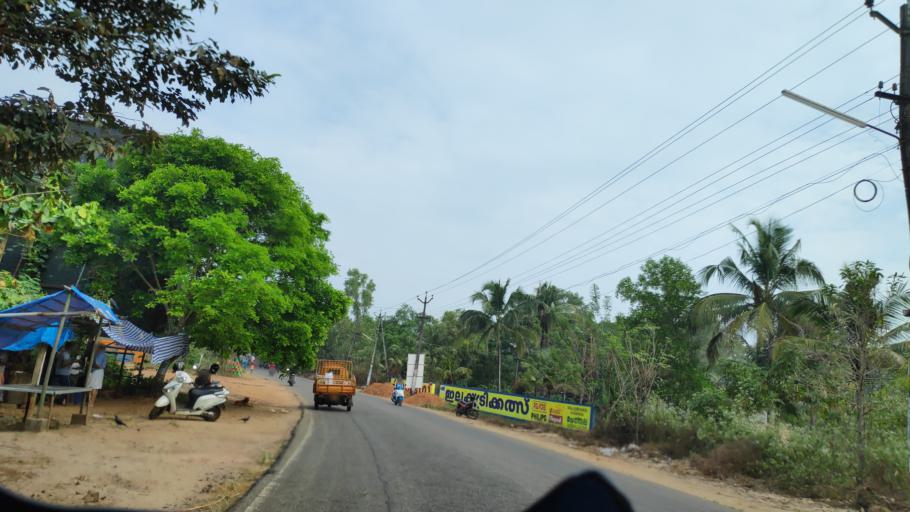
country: IN
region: Kerala
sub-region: Alappuzha
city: Vayalar
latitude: 9.7223
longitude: 76.3606
